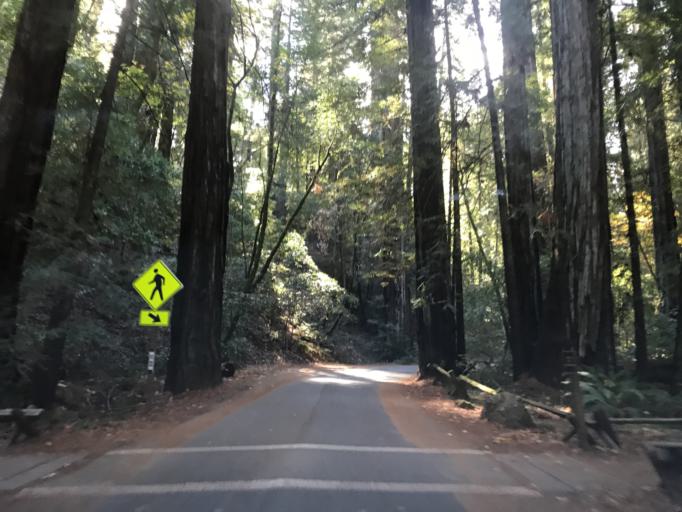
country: US
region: California
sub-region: Sonoma County
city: Guerneville
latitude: 38.5409
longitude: -123.0033
